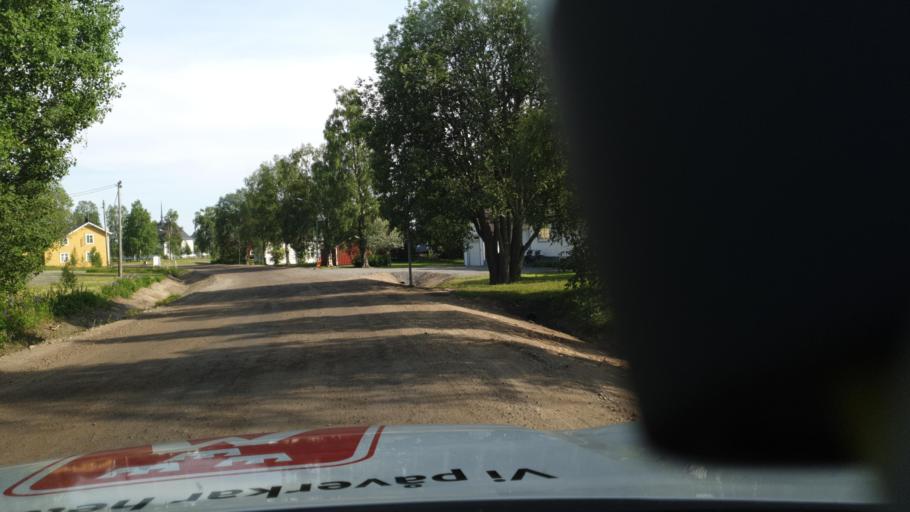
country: SE
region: Vaesterbotten
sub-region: Robertsfors Kommun
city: Robertsfors
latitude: 64.2839
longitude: 21.0362
